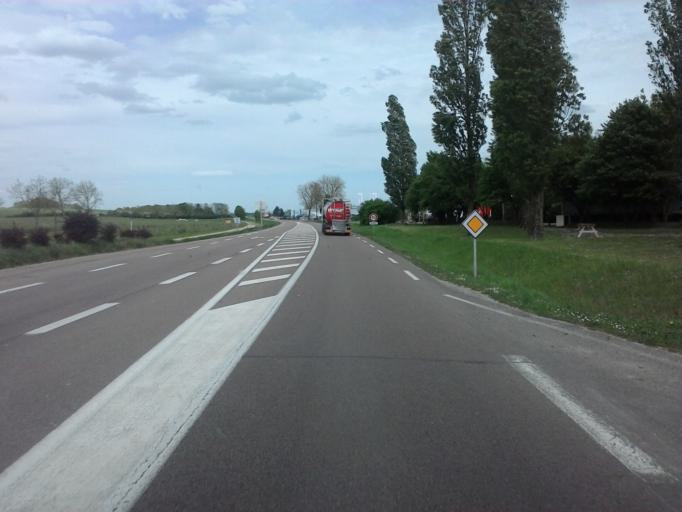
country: FR
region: Bourgogne
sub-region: Departement de l'Yonne
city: Saint-Florentin
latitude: 48.0093
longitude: 3.7490
